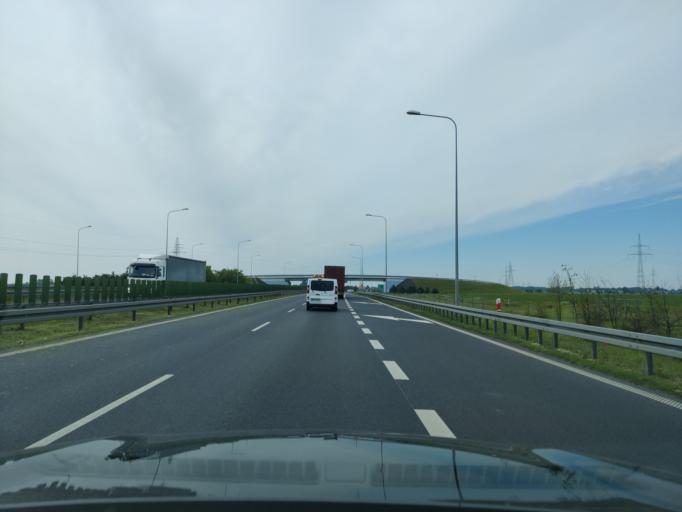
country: PL
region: Greater Poland Voivodeship
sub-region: Powiat poznanski
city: Komorniki
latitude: 52.3455
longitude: 16.7545
